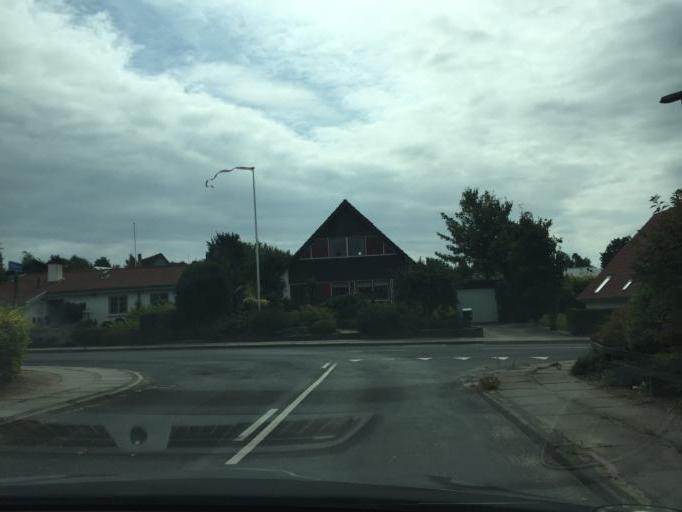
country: DK
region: South Denmark
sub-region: Assens Kommune
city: Arup
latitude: 55.3766
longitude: 10.0409
